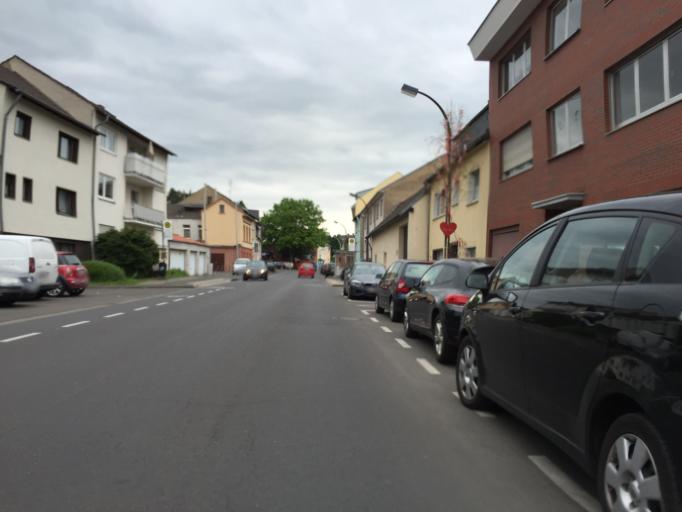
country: DE
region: North Rhine-Westphalia
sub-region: Regierungsbezirk Koln
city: Bonn
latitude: 50.7134
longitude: 7.0712
